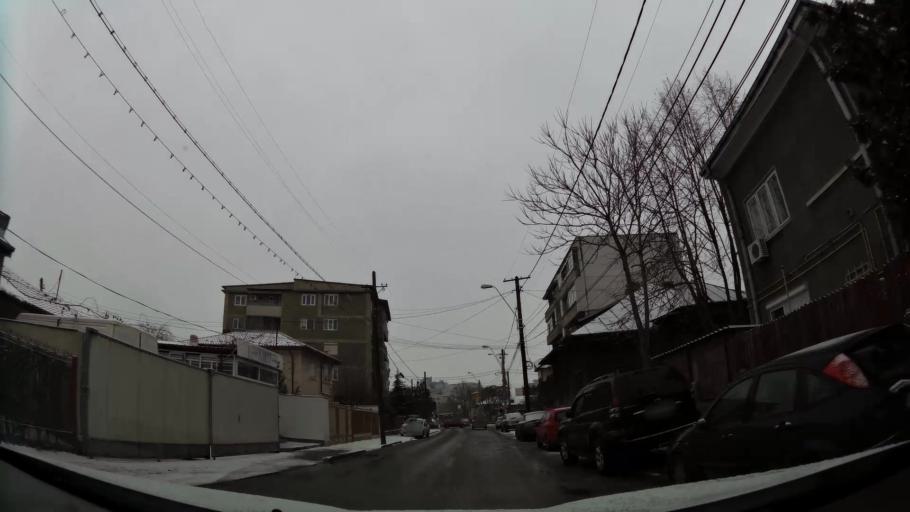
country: RO
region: Prahova
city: Ploiesti
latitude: 44.9379
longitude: 26.0174
